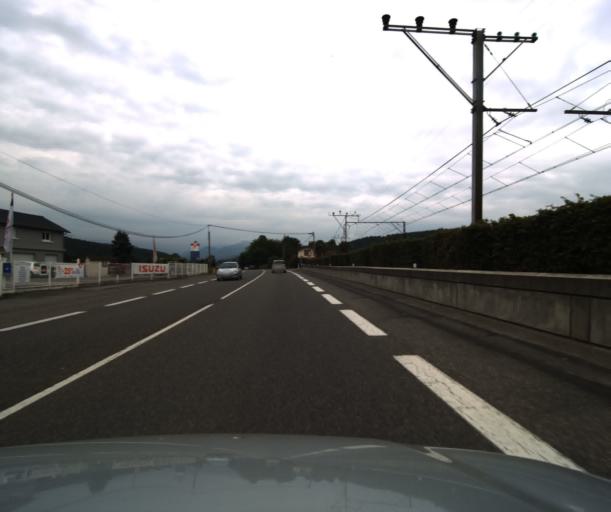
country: FR
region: Midi-Pyrenees
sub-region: Departement des Hautes-Pyrenees
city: Ossun
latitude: 43.1570
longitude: -0.0197
